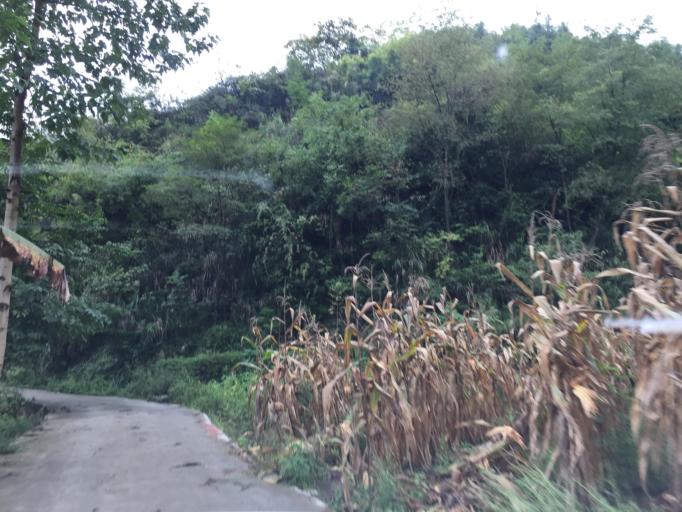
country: CN
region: Guizhou Sheng
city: Longquan
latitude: 28.2121
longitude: 108.0545
